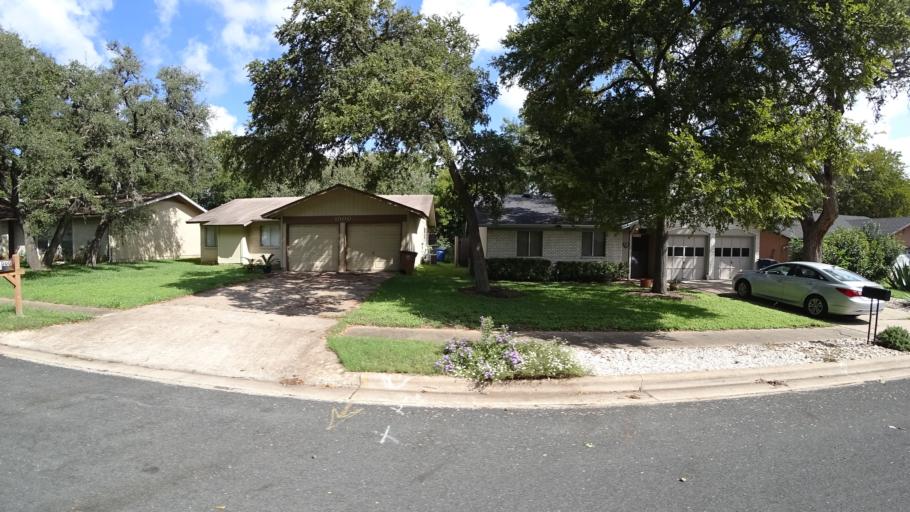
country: US
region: Texas
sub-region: Travis County
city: Onion Creek
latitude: 30.1977
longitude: -97.7937
